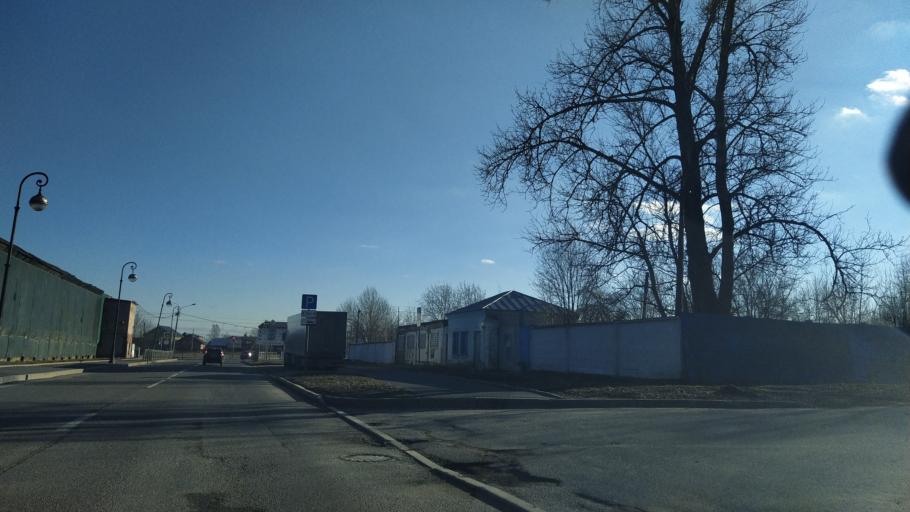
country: RU
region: St.-Petersburg
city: Pushkin
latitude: 59.7018
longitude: 30.3938
